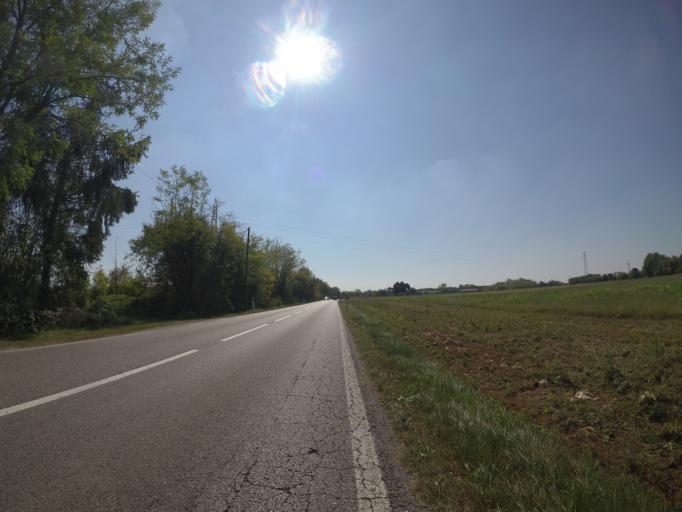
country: IT
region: Friuli Venezia Giulia
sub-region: Provincia di Udine
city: Codroipo
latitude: 45.9811
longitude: 12.9931
